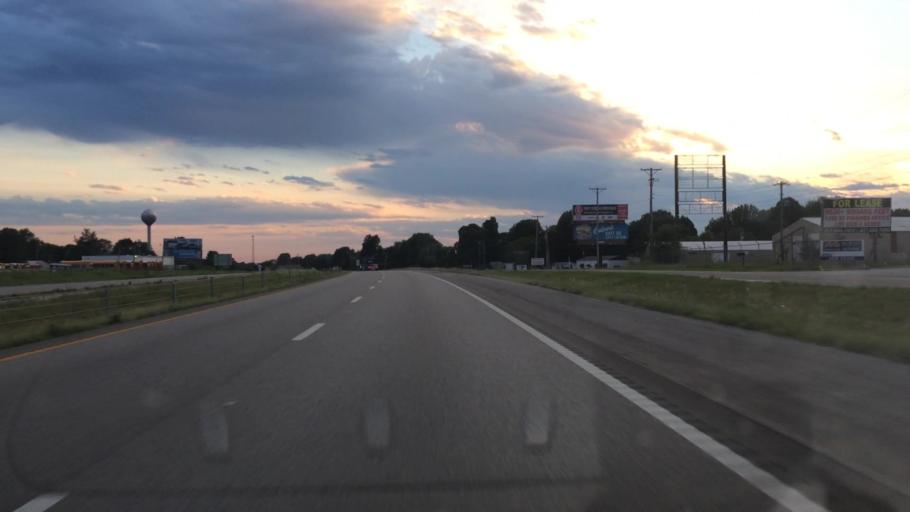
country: US
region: Missouri
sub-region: Greene County
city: Strafford
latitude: 37.2728
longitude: -93.1200
